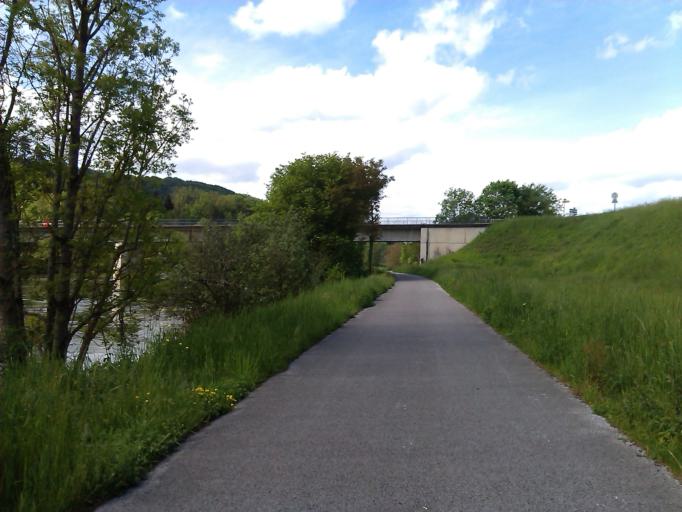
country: FR
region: Franche-Comte
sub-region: Departement du Doubs
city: Novillars
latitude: 47.2865
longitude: 6.1502
